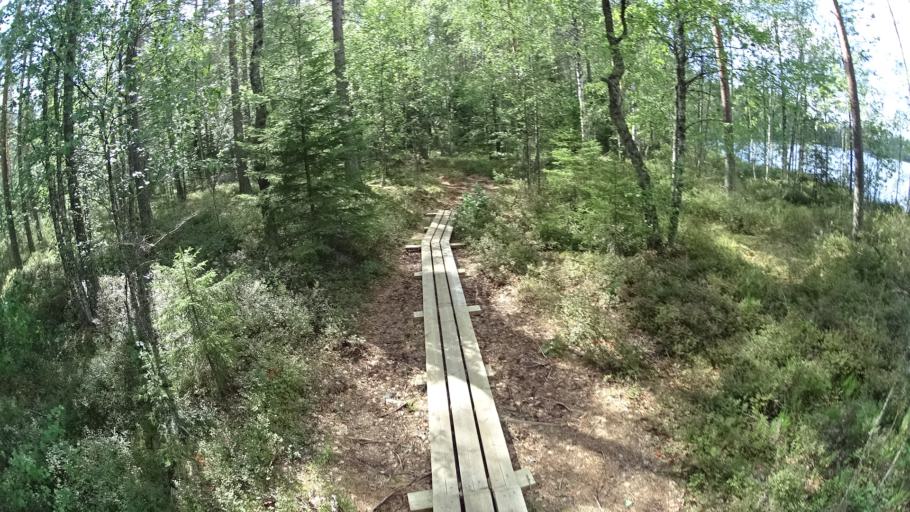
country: FI
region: Uusimaa
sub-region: Helsinki
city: Kaerkoelae
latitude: 60.7330
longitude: 24.0780
